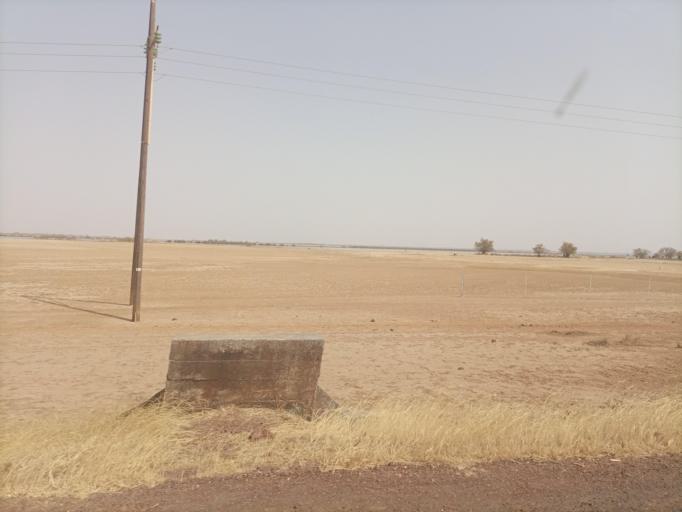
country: SN
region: Fatick
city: Foundiougne
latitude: 14.1747
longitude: -16.4592
